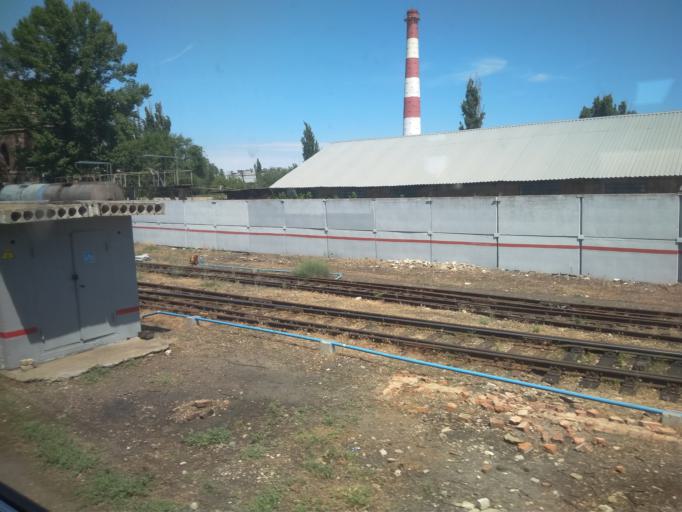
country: RU
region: Volgograd
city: Volgograd
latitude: 48.5230
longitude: 44.5053
